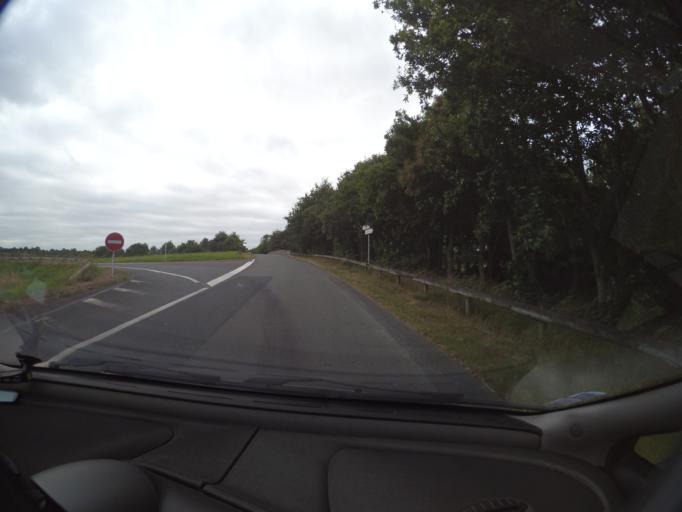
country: FR
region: Pays de la Loire
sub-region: Departement de la Vendee
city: Saint-Hilaire-de-Loulay
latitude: 47.0046
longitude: -1.3415
